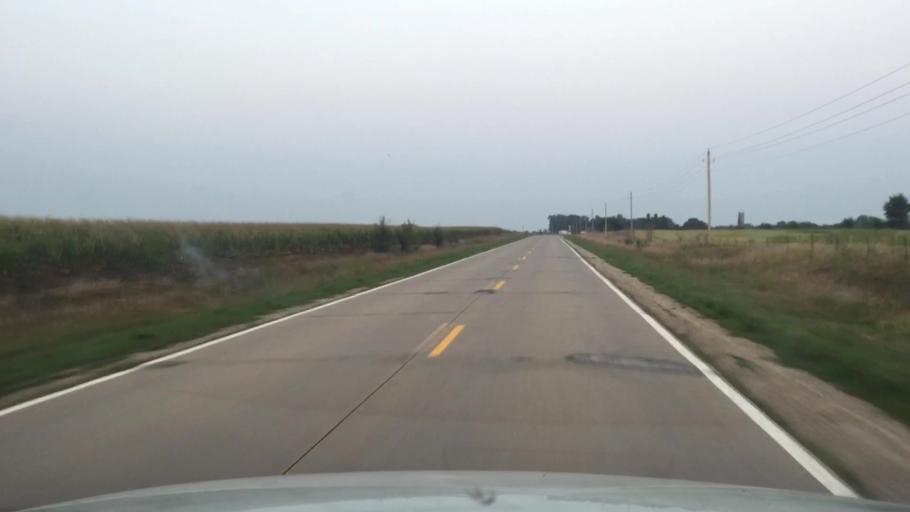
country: US
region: Iowa
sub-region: Clarke County
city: Osceola
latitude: 41.1875
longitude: -93.6863
